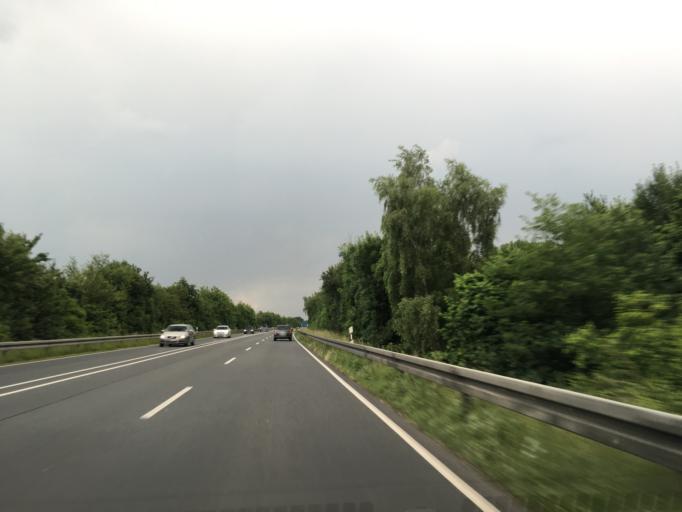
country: DE
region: North Rhine-Westphalia
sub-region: Regierungsbezirk Munster
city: Ochtrup
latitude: 52.1883
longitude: 7.2268
